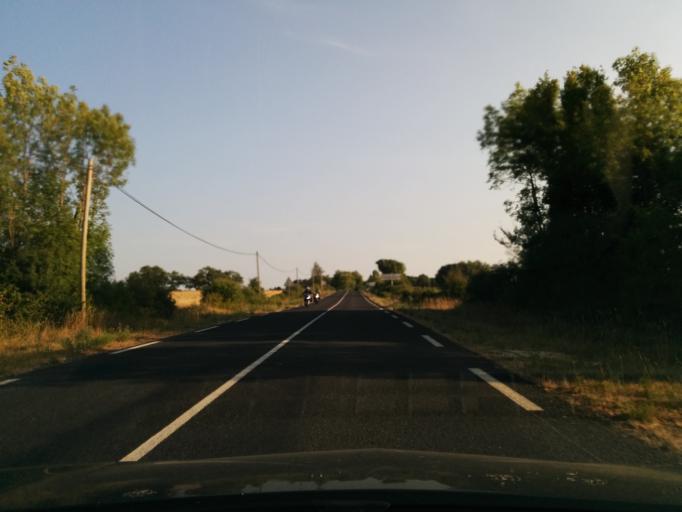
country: FR
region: Midi-Pyrenees
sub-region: Departement du Lot
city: Le Vigan
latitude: 44.7365
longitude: 1.5007
